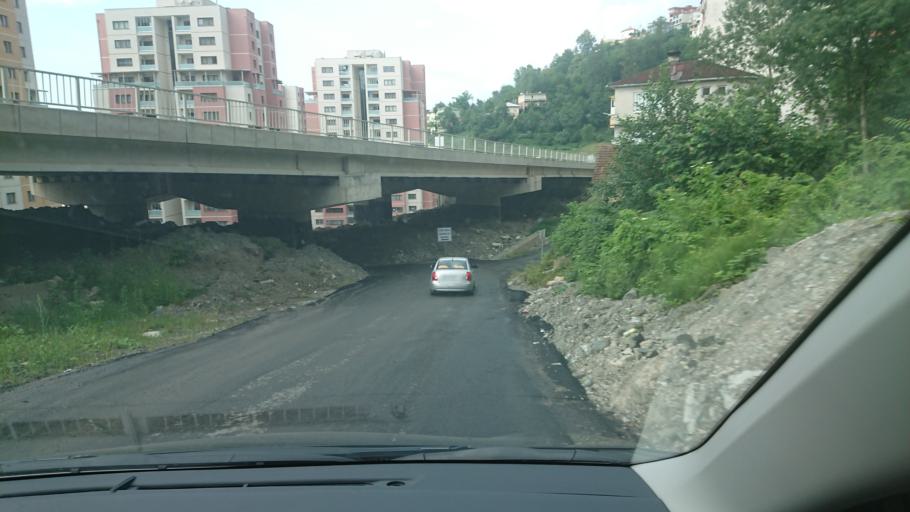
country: TR
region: Rize
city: Rize
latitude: 41.0148
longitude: 40.5155
